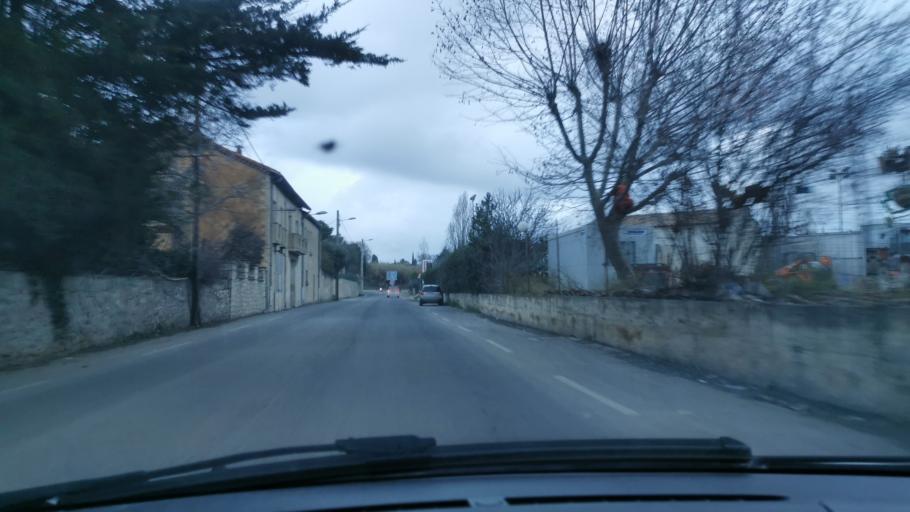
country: FR
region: Languedoc-Roussillon
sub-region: Departement de l'Herault
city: Montpellier
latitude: 43.5835
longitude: 3.8696
